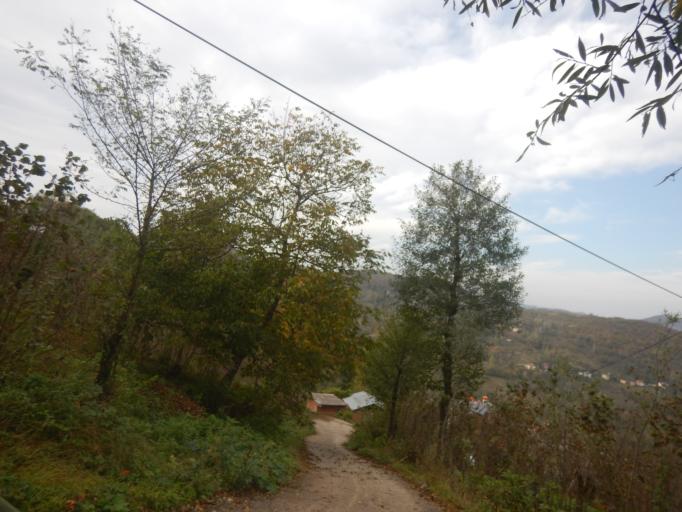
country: TR
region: Ordu
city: Golkoy
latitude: 40.6915
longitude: 37.5849
